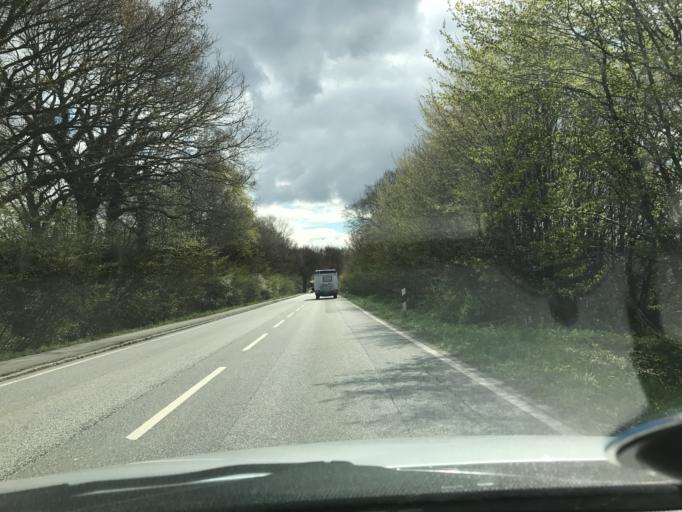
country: DE
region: Schleswig-Holstein
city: Susel
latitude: 54.0937
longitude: 10.6796
